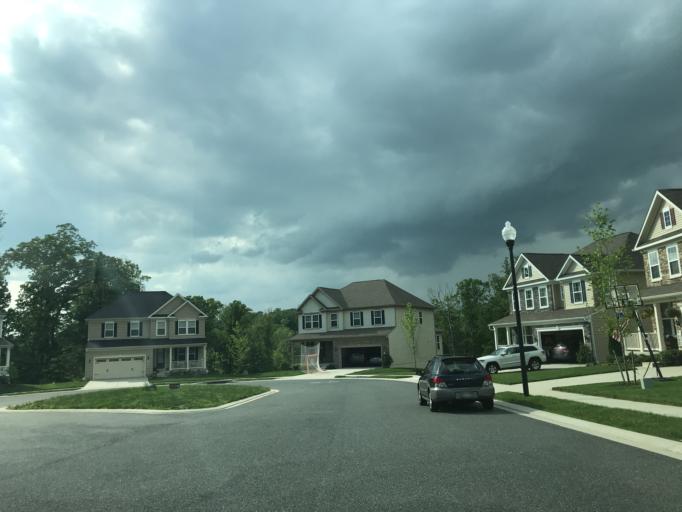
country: US
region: Maryland
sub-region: Harford County
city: Bel Air North
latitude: 39.5504
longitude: -76.3865
